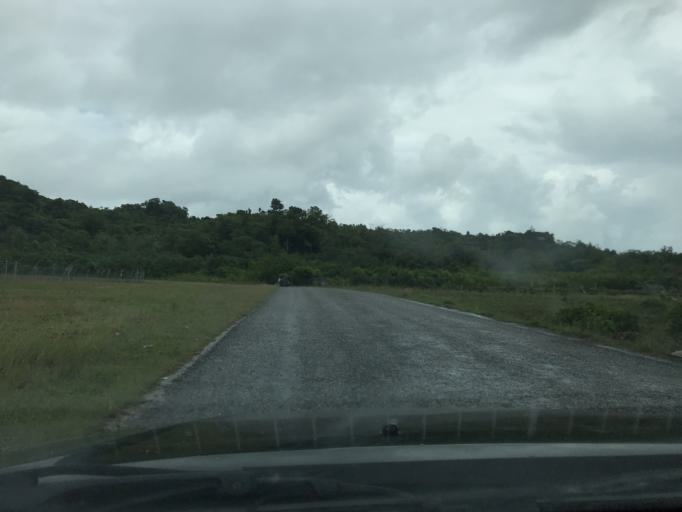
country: SB
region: Western Province
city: Gizo
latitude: -8.3257
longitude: 157.2729
